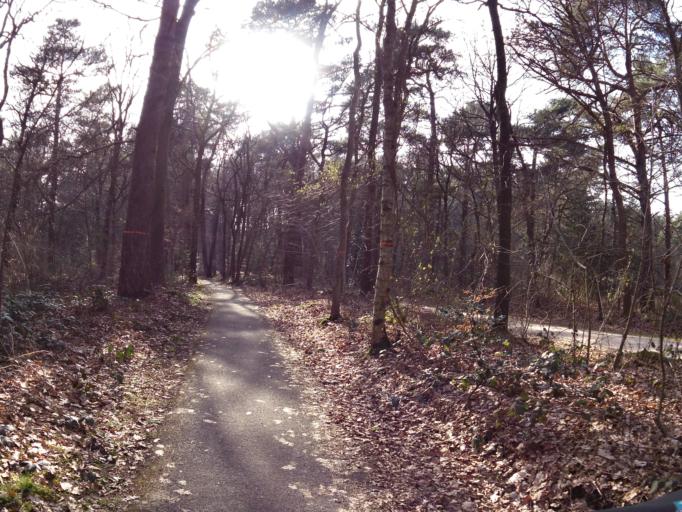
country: NL
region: Overijssel
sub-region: Gemeente Steenwijkerland
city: Tuk
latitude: 52.8111
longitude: 6.1105
